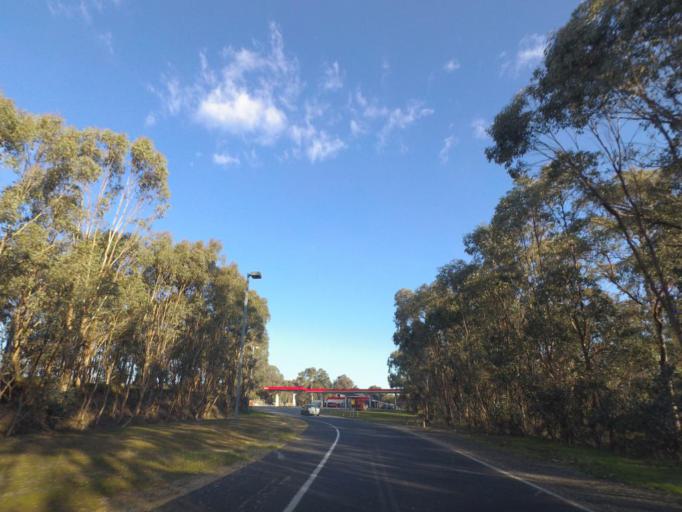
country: AU
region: Victoria
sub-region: Murrindindi
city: Kinglake West
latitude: -37.0621
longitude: 145.1015
